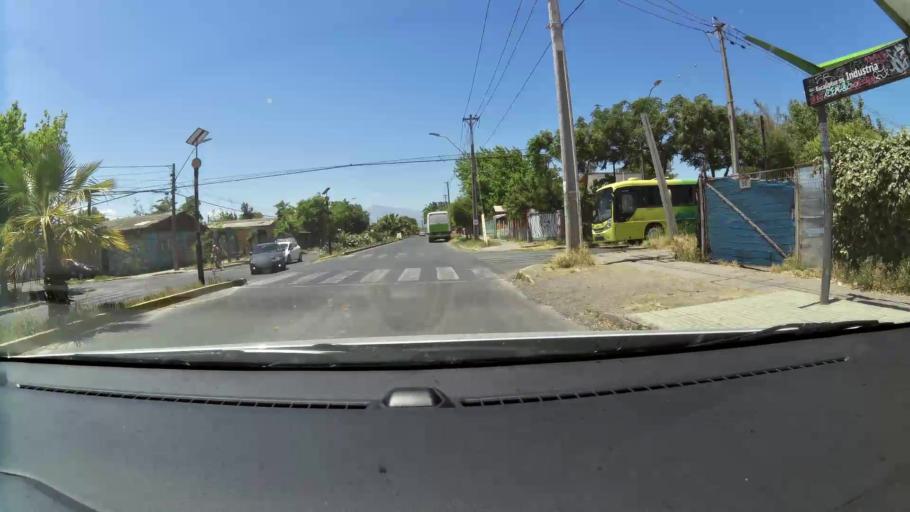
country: CL
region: Santiago Metropolitan
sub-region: Provincia de Maipo
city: San Bernardo
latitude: -33.6094
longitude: -70.7015
